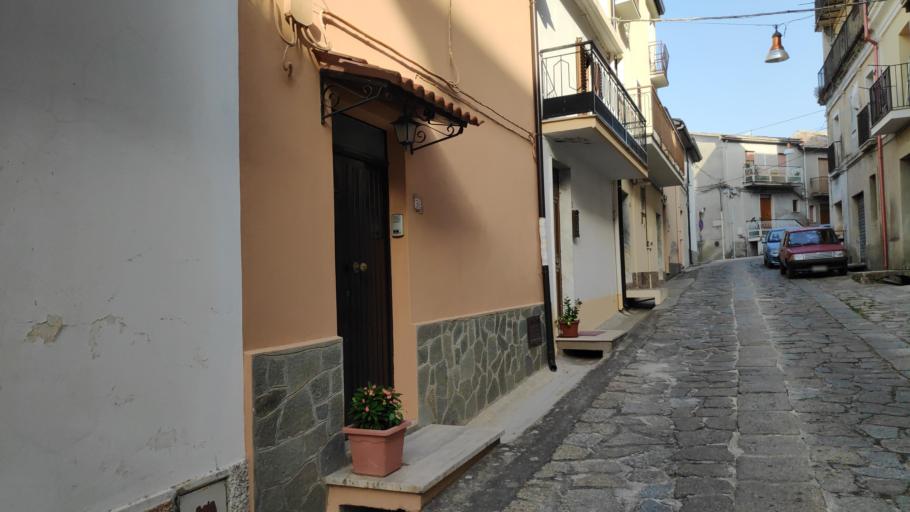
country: IT
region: Calabria
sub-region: Provincia di Catanzaro
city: Sant'Andrea Apostolo dello Ionio
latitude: 38.6209
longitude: 16.5312
